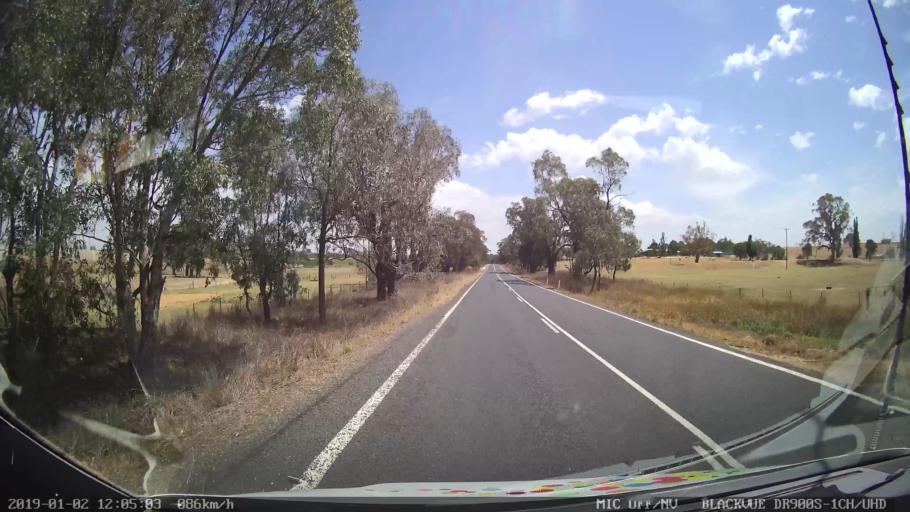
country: AU
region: New South Wales
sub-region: Young
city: Young
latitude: -34.5188
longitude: 148.3045
